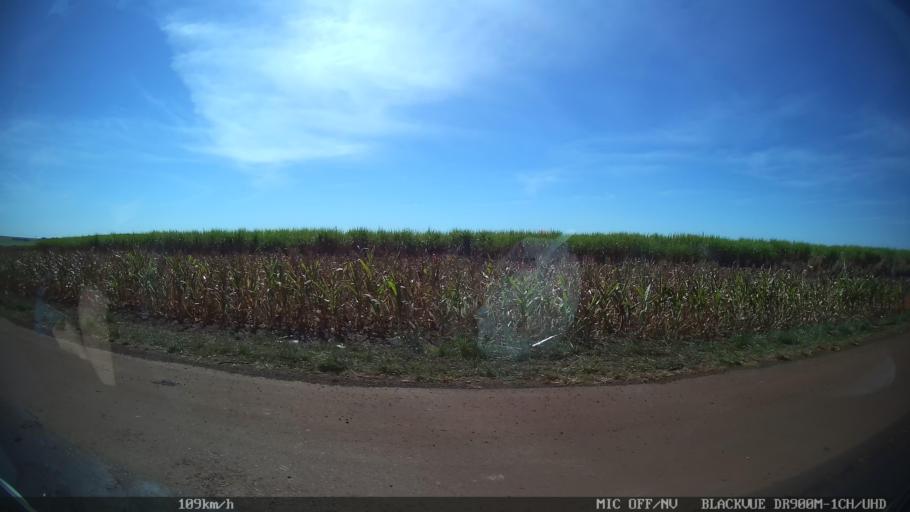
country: BR
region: Sao Paulo
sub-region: Ipua
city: Ipua
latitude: -20.4946
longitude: -47.9782
